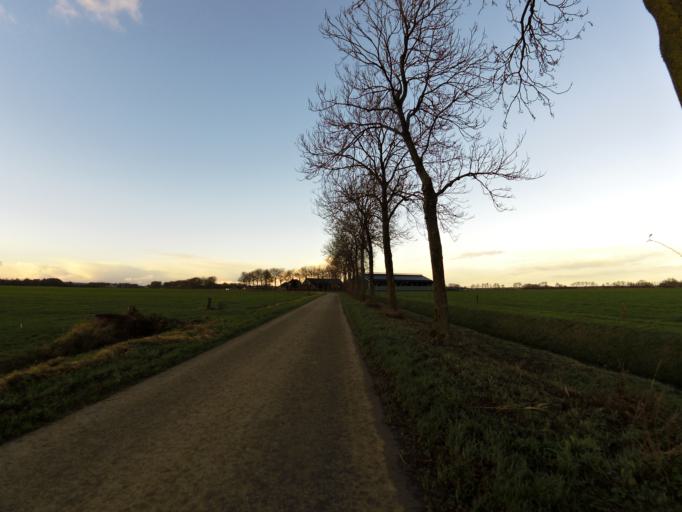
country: NL
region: Gelderland
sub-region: Oude IJsselstreek
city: Gendringen
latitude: 51.8724
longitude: 6.3219
